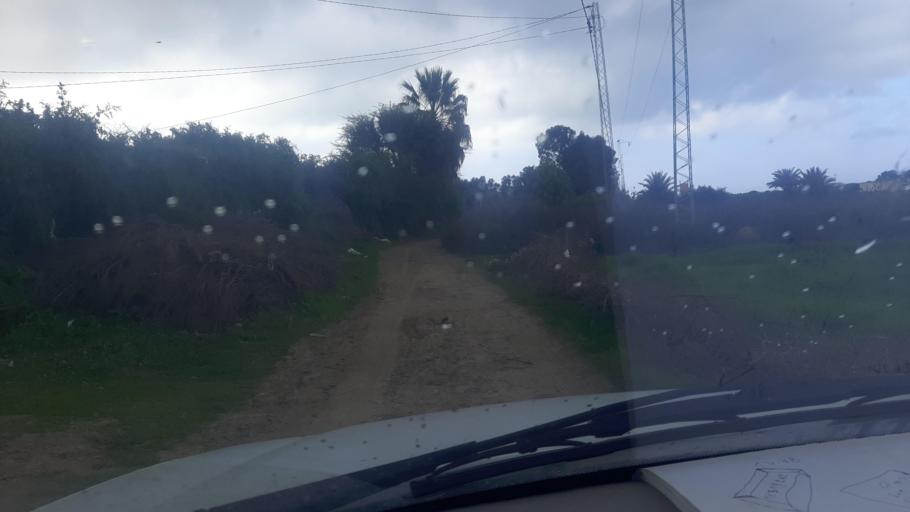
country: TN
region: Nabul
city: Manzil Bu Zalafah
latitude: 36.7389
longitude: 10.5218
